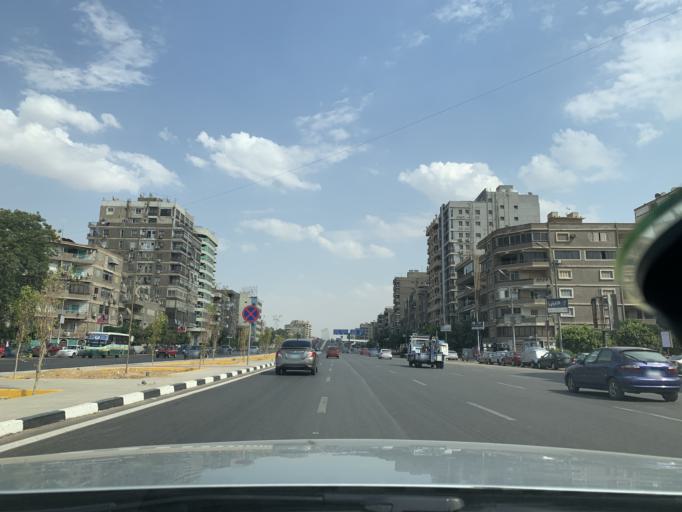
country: EG
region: Muhafazat al Qalyubiyah
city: Al Khankah
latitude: 30.1151
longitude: 31.3430
